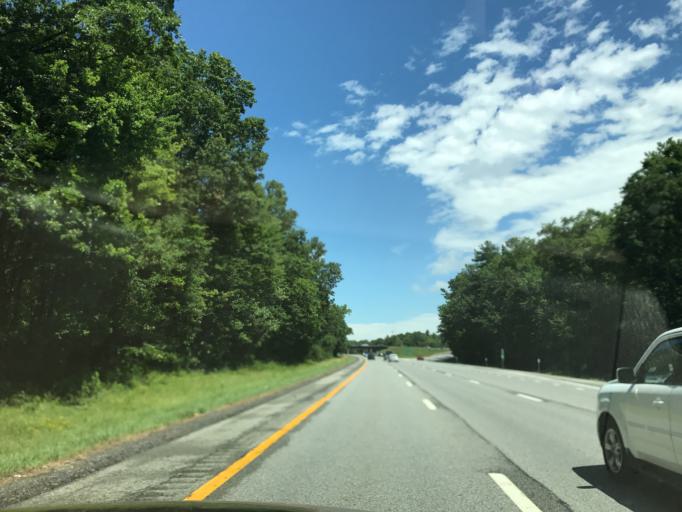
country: US
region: New York
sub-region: Saratoga County
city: Saratoga Springs
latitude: 43.1655
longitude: -73.7150
